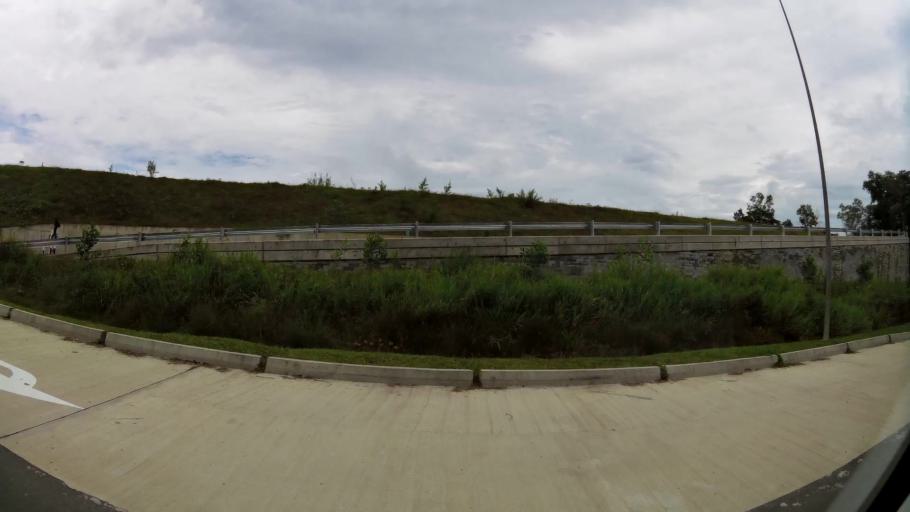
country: BN
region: Brunei and Muara
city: Bandar Seri Begawan
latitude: 4.8824
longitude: 114.9147
